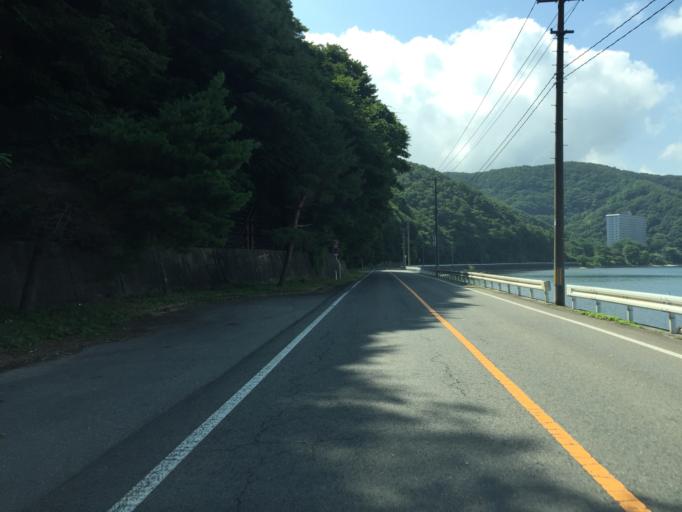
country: JP
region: Fukushima
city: Inawashiro
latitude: 37.4665
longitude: 140.1541
